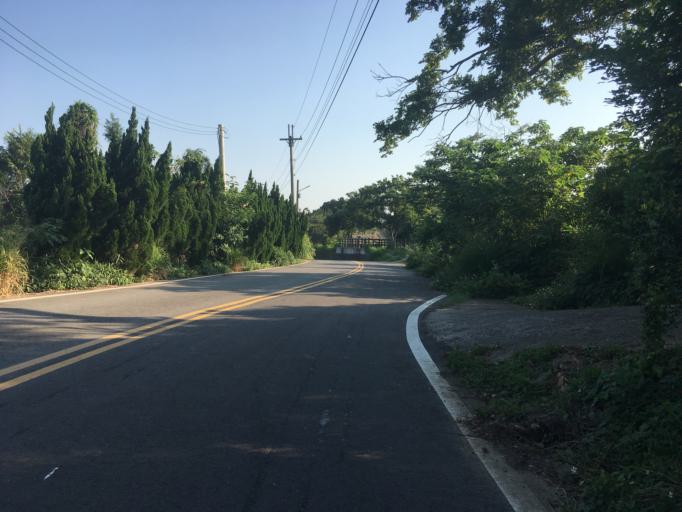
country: TW
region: Taiwan
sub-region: Hsinchu
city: Hsinchu
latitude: 24.7315
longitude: 120.9886
